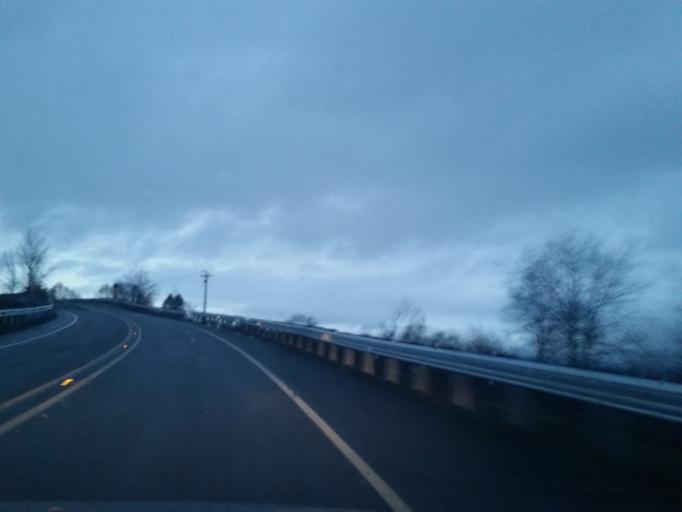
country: US
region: Washington
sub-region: Snohomish County
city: Fobes Hill
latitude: 47.9474
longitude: -122.1586
